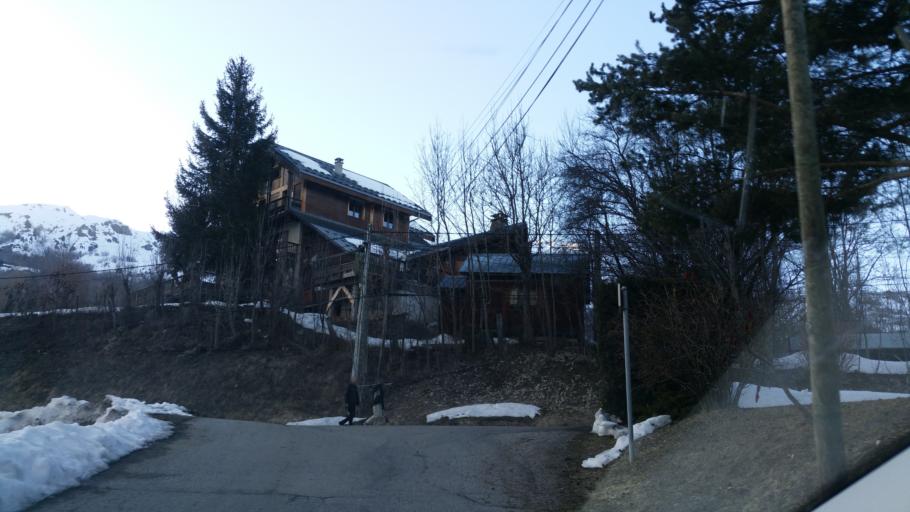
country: FR
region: Rhone-Alpes
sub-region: Departement de la Savoie
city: Saint-Jean-de-Maurienne
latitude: 45.2665
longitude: 6.2977
